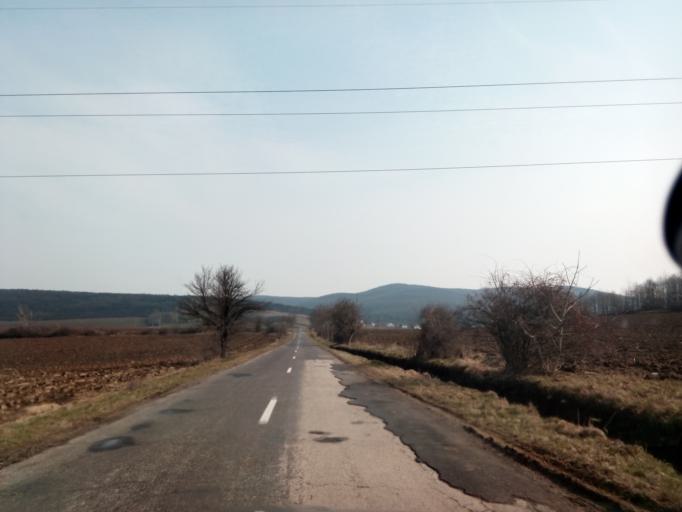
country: HU
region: Borsod-Abauj-Zemplen
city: Satoraljaujhely
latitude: 48.4707
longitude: 21.6625
